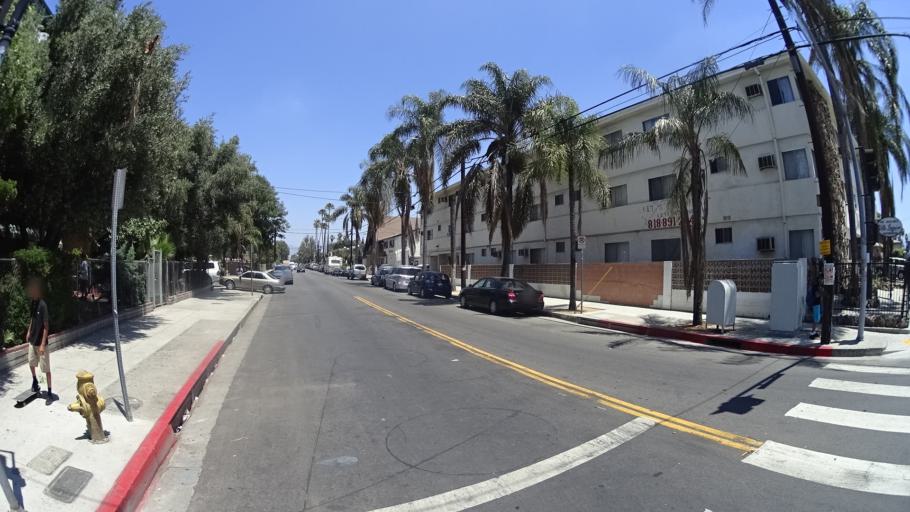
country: US
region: California
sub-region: Los Angeles County
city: Van Nuys
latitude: 34.2217
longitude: -118.4554
